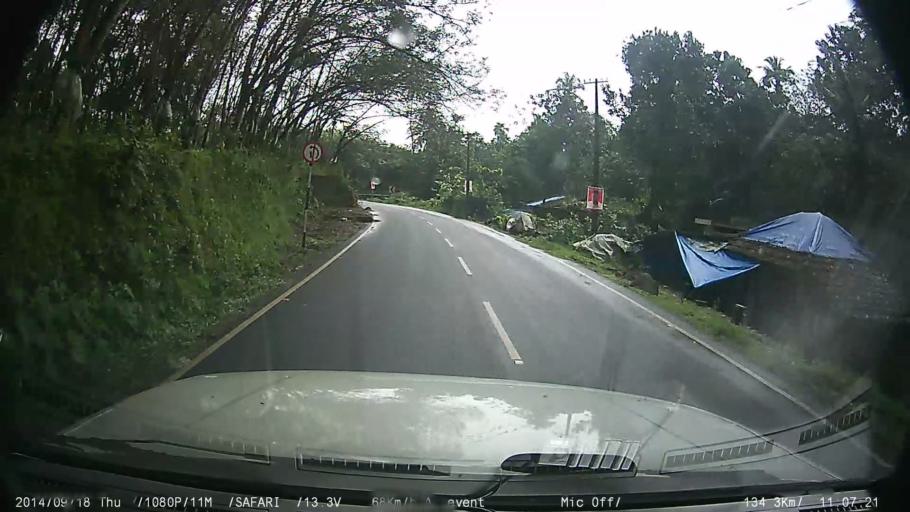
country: IN
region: Kerala
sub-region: Ernakulam
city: Muvattupuzha
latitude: 9.8838
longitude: 76.5989
